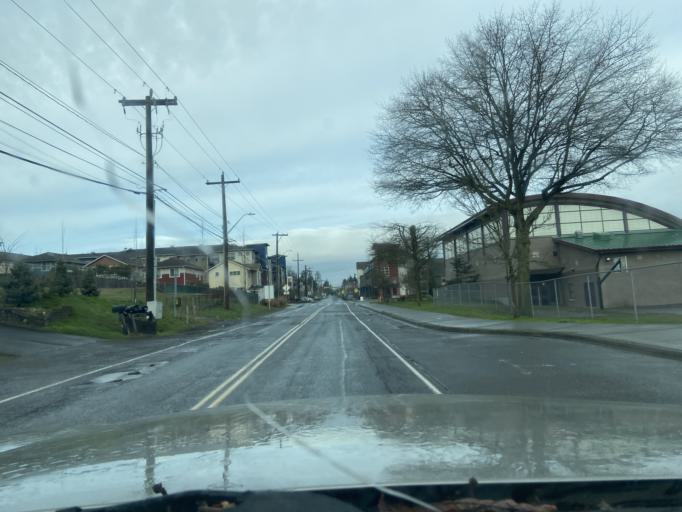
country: US
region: Washington
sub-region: King County
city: White Center
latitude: 47.5128
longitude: -122.3450
